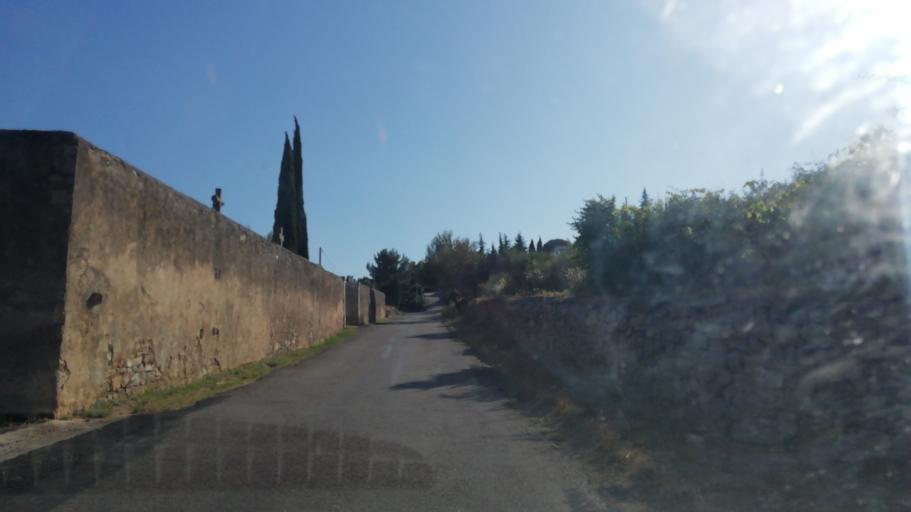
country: FR
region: Languedoc-Roussillon
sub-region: Departement de l'Herault
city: Nebian
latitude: 43.6111
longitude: 3.4341
